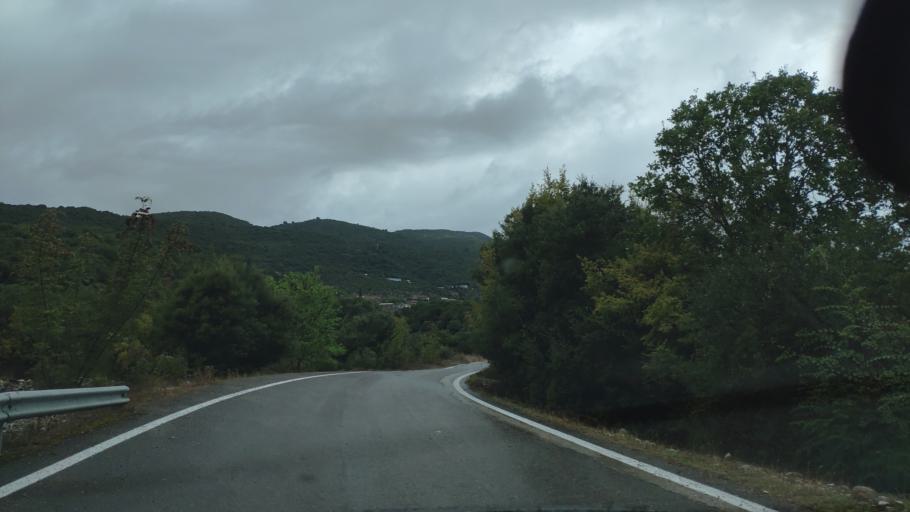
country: GR
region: Central Greece
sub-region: Nomos Evrytanias
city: Kerasochori
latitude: 39.1077
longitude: 21.4188
